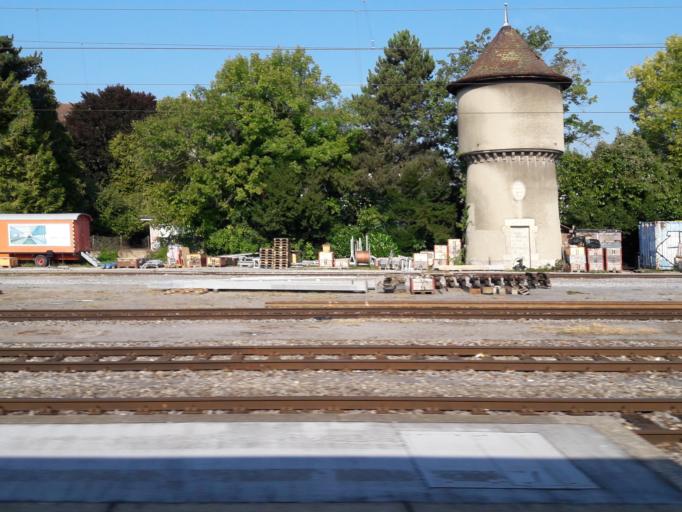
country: CH
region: Vaud
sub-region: Nyon District
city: Nyon
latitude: 46.3863
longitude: 6.2381
